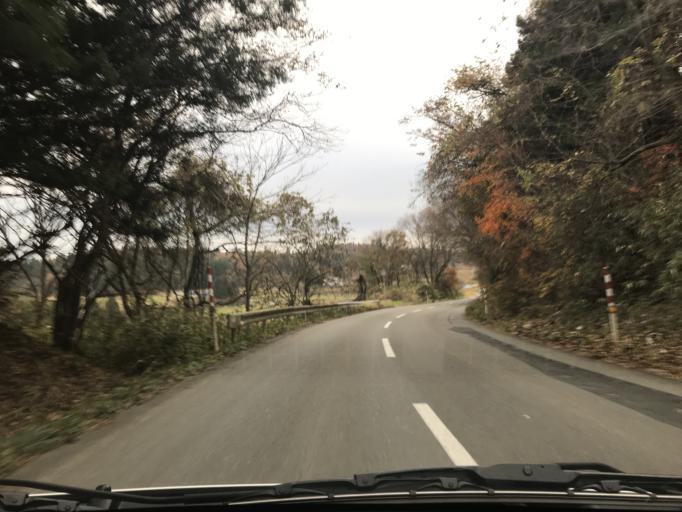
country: JP
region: Iwate
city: Kitakami
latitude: 39.2510
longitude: 141.2678
